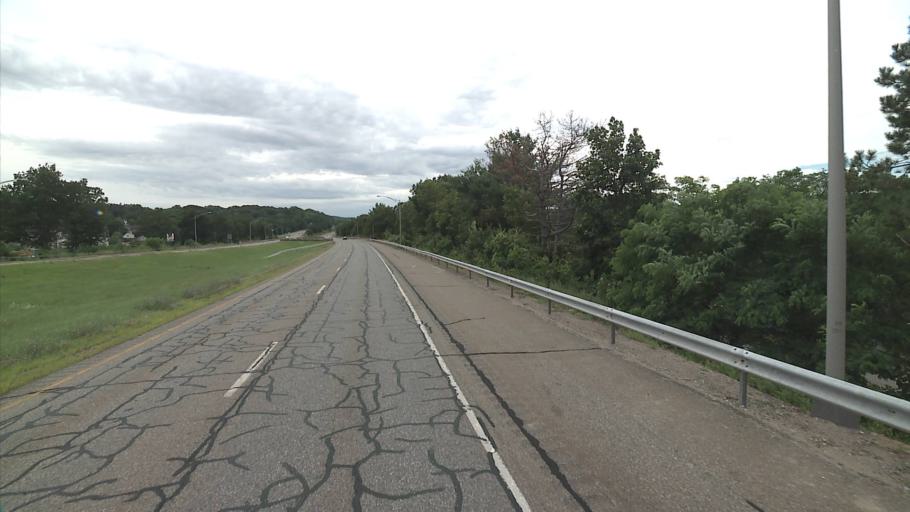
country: US
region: Connecticut
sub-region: Litchfield County
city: Torrington
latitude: 41.8091
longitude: -73.1139
